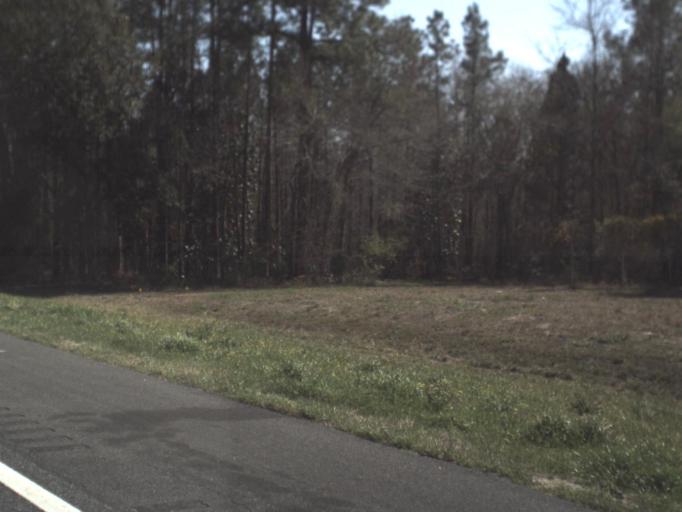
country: US
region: Florida
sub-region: Jackson County
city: Marianna
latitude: 30.7024
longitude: -85.1390
